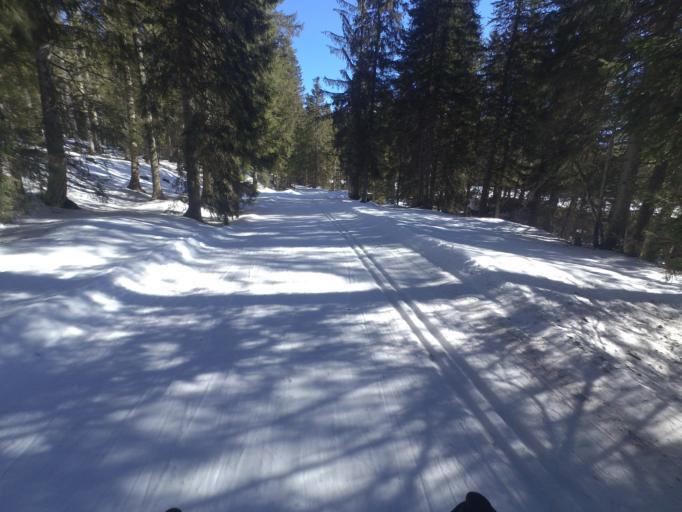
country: AT
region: Upper Austria
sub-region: Politischer Bezirk Gmunden
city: Sankt Wolfgang im Salzkammergut
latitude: 47.6491
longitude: 13.4145
